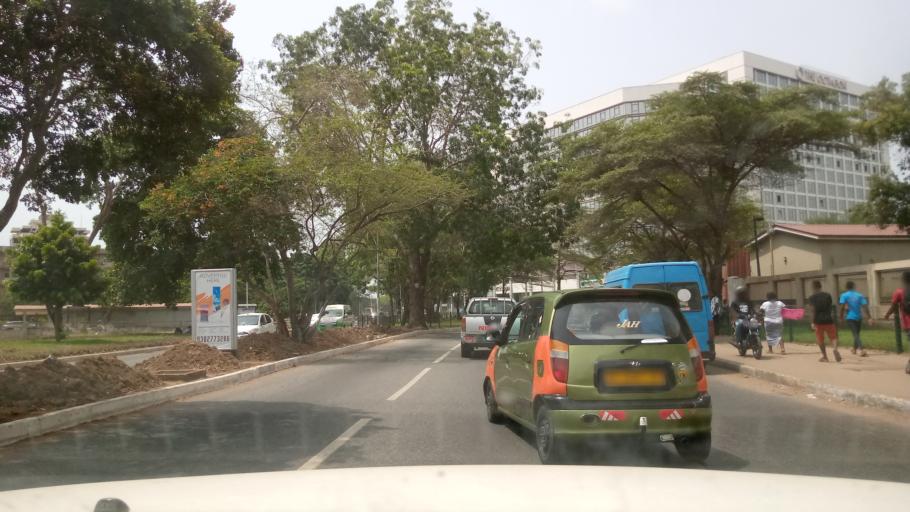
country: GH
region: Greater Accra
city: Accra
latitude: 5.5531
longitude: -0.2021
